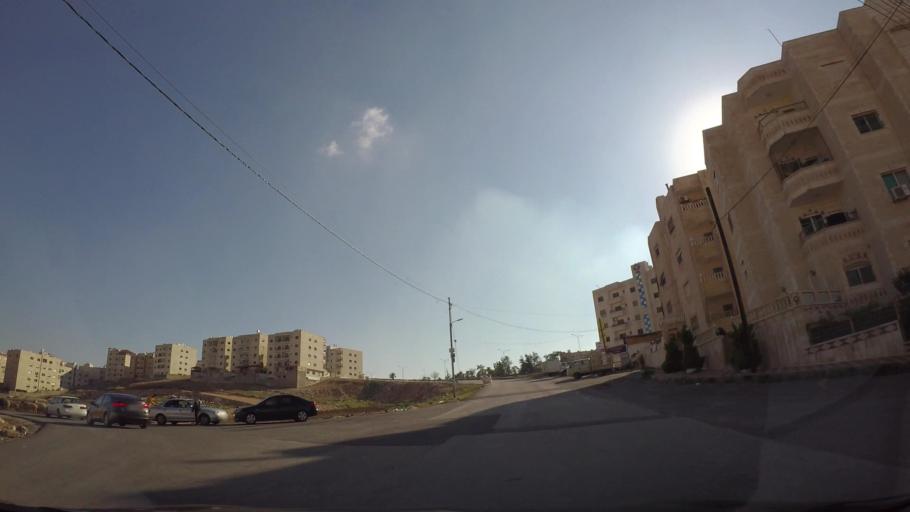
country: JO
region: Amman
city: Amman
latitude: 31.9770
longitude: 35.9350
